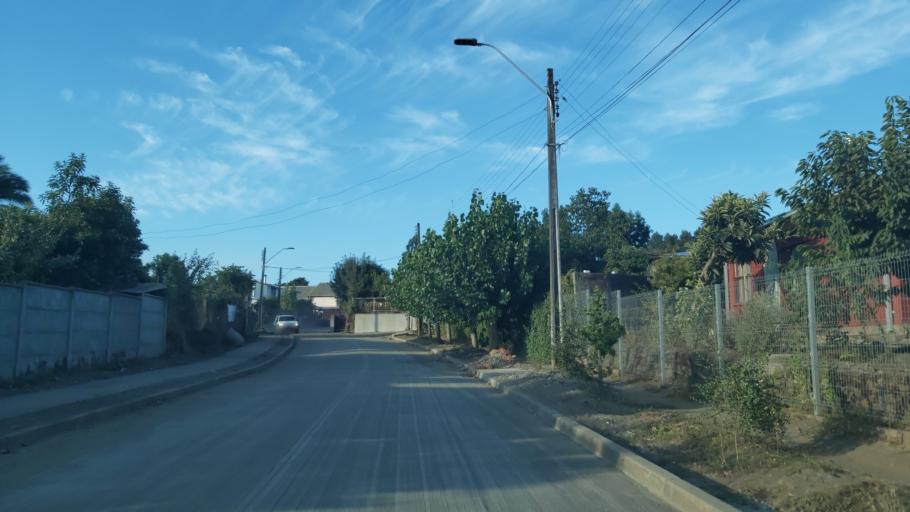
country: CL
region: Biobio
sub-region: Provincia de Biobio
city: La Laja
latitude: -37.1617
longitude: -72.9117
